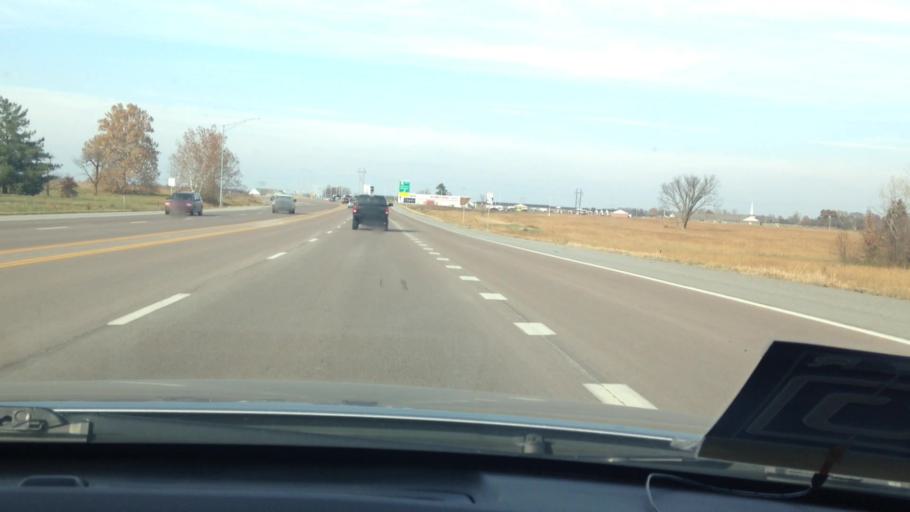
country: US
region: Missouri
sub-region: Henry County
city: Clinton
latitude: 38.3786
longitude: -93.7515
